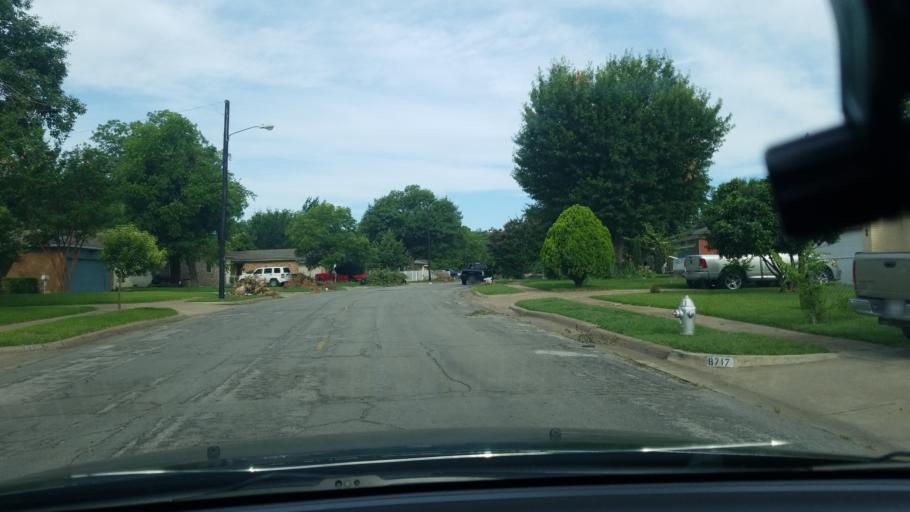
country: US
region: Texas
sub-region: Dallas County
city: Balch Springs
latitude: 32.7544
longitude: -96.6719
